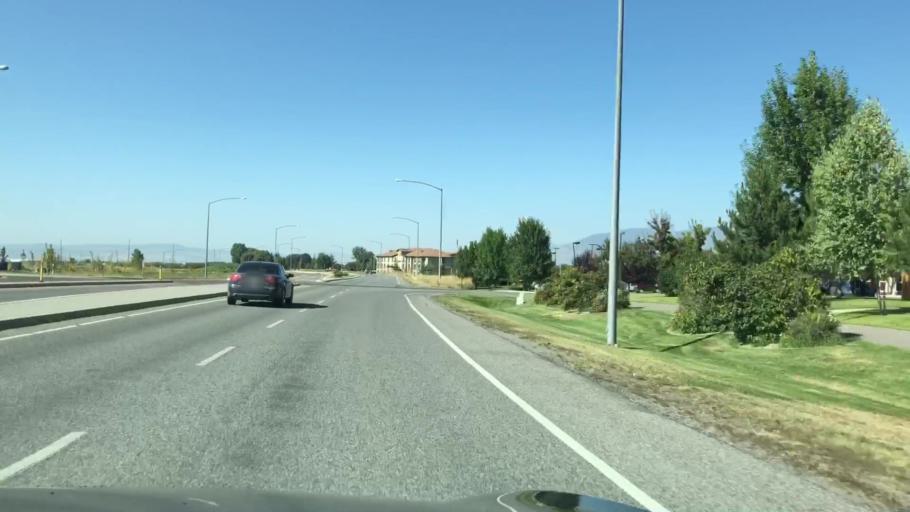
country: US
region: Montana
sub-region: Gallatin County
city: Bozeman
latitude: 45.7143
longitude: -111.0683
